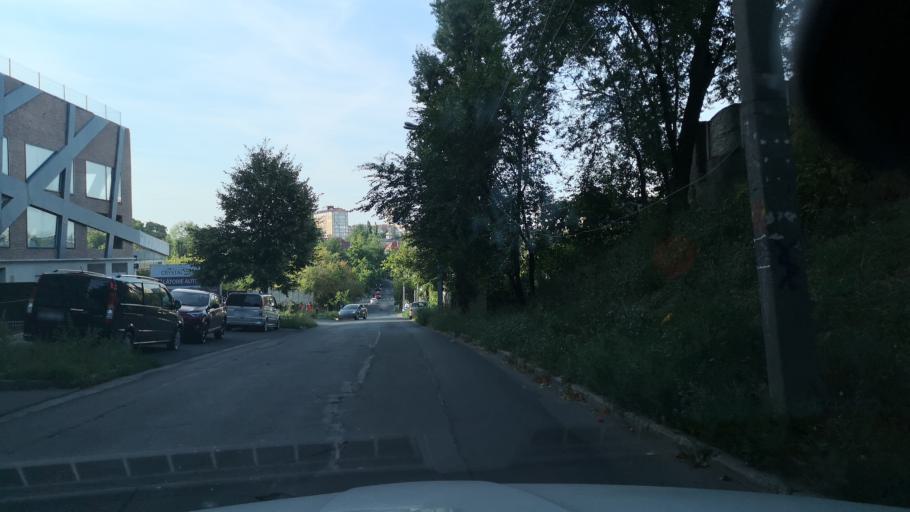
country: MD
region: Chisinau
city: Chisinau
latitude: 47.0087
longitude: 28.8487
